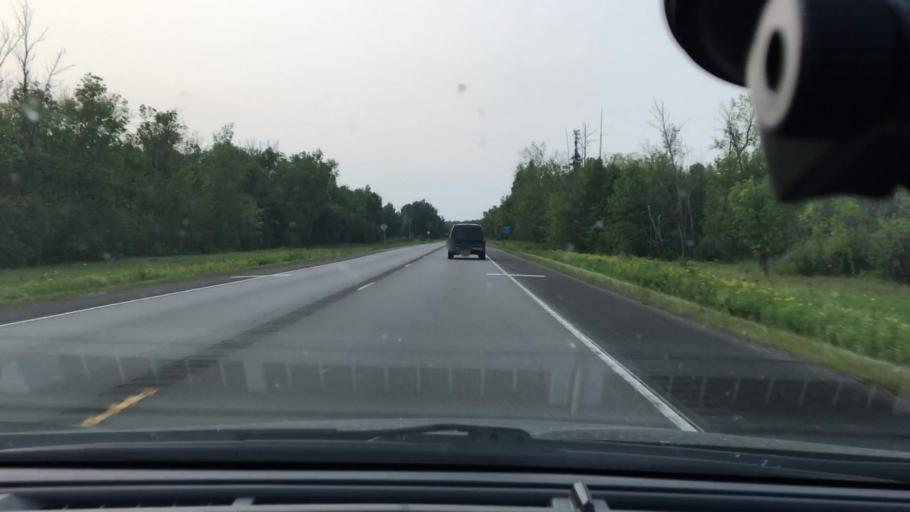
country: US
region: Minnesota
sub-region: Mille Lacs County
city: Vineland
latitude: 46.3194
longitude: -93.8386
